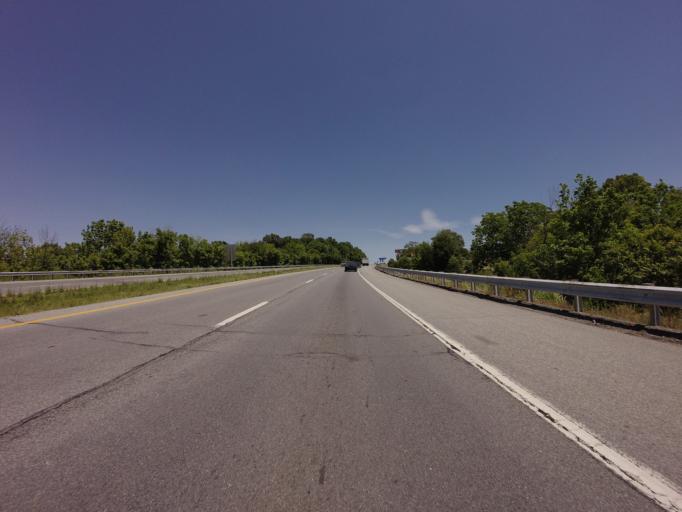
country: US
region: West Virginia
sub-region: Jefferson County
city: Bolivar
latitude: 39.3176
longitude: -77.7678
